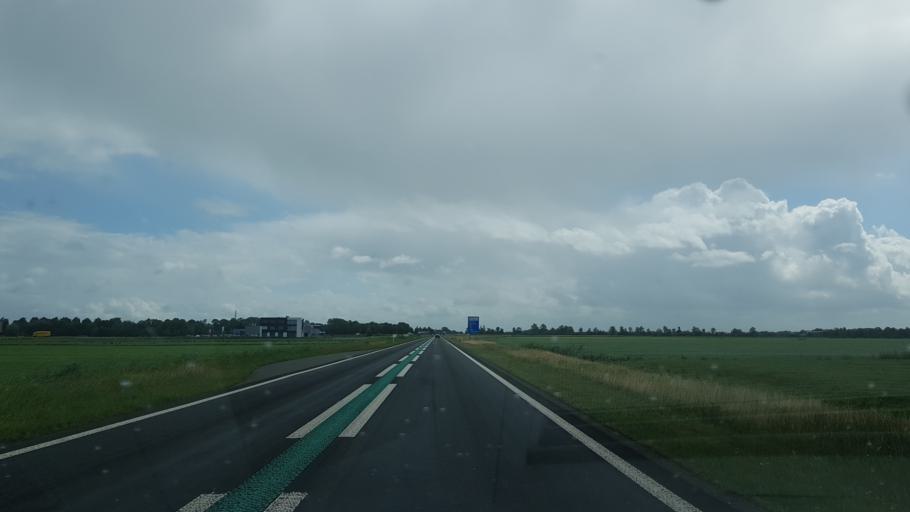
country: NL
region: Friesland
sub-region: Gemeente Dongeradeel
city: Dokkum
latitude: 53.3096
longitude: 5.9821
